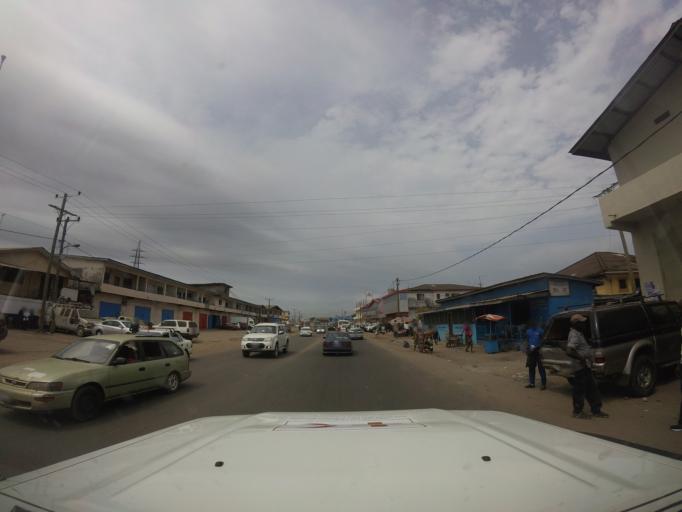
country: LR
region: Montserrado
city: Monrovia
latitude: 6.3489
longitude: -10.7878
